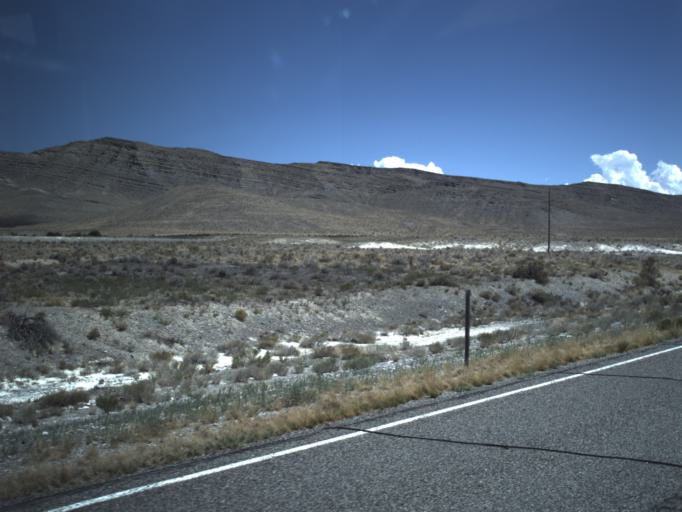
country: US
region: Utah
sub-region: Beaver County
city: Milford
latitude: 39.0376
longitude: -113.3952
